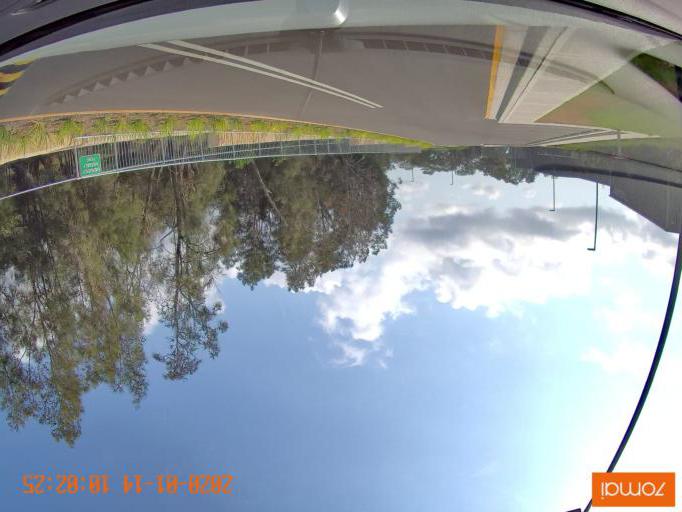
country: AU
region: New South Wales
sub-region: Wyong Shire
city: Kingfisher Shores
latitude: -33.1228
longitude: 151.5400
